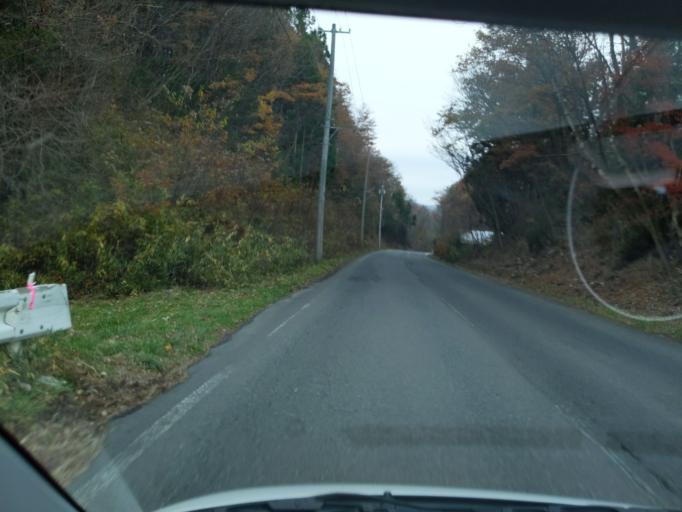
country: JP
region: Iwate
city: Kitakami
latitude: 39.2472
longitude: 141.2155
